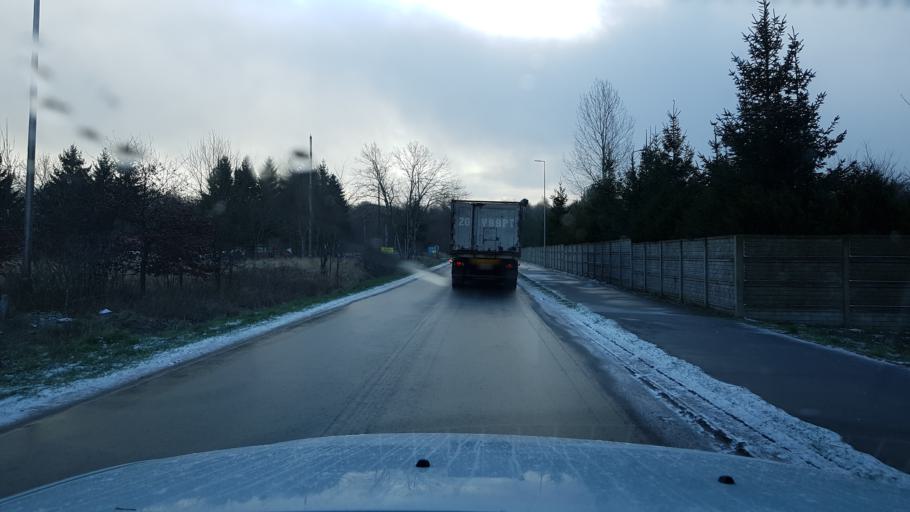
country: PL
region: West Pomeranian Voivodeship
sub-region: Powiat gryficki
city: Trzebiatow
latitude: 54.0511
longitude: 15.3076
